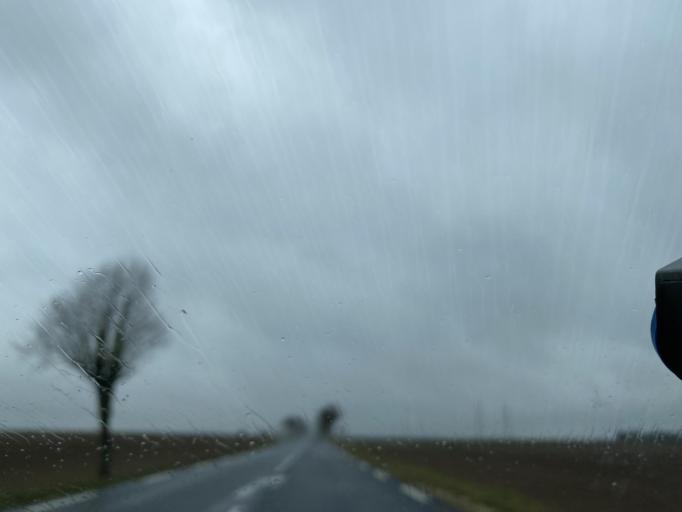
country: FR
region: Centre
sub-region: Departement d'Eure-et-Loir
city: Baigneaux
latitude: 48.1724
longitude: 1.8365
